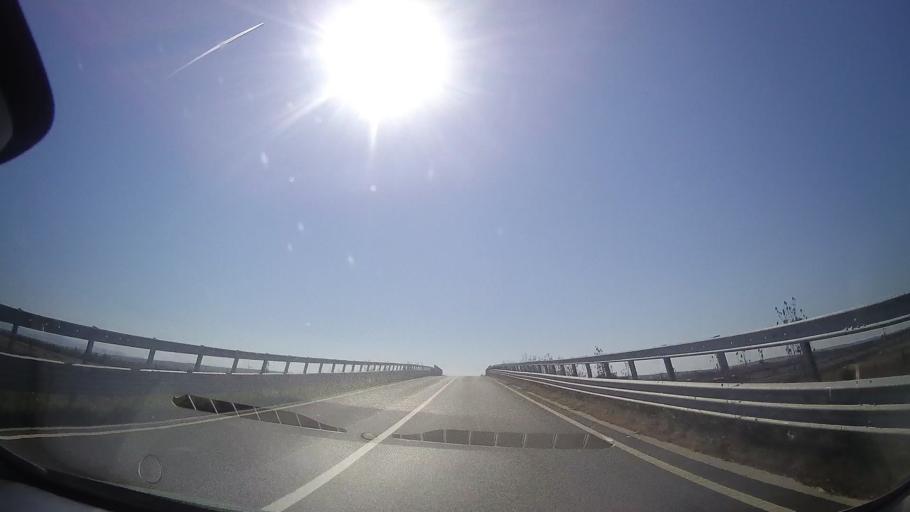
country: RO
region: Timis
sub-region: Comuna Bethausen
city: Bethausen
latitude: 45.8164
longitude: 21.9594
